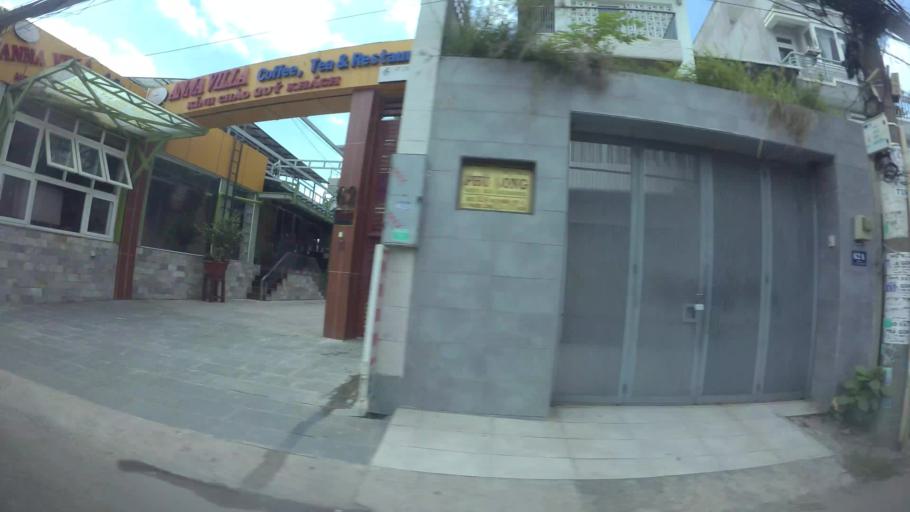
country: VN
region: Ho Chi Minh City
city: Quan Chin
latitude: 10.8228
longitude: 106.7610
